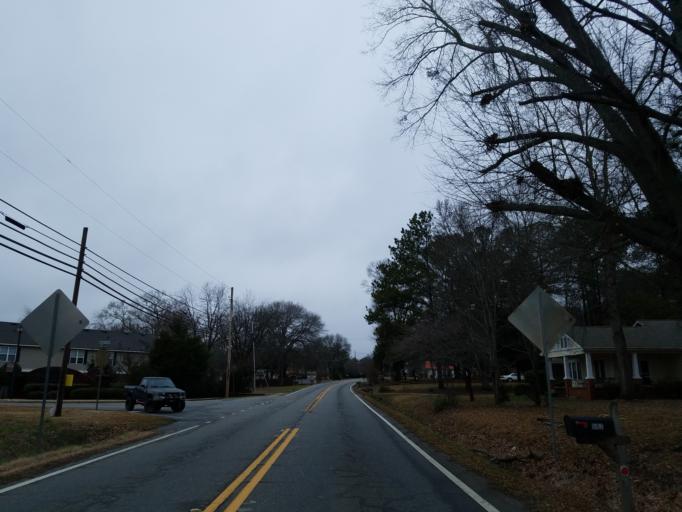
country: US
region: Georgia
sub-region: Bartow County
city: Cartersville
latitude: 34.1911
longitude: -84.8206
